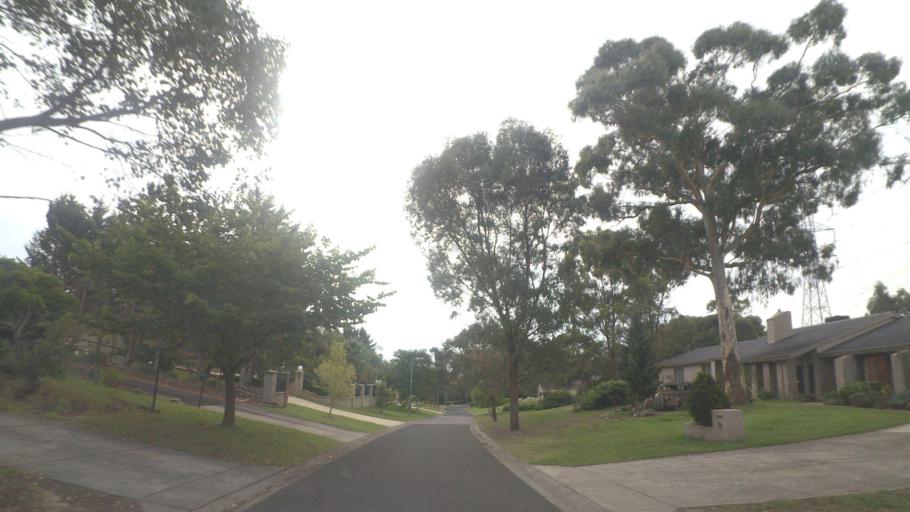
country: AU
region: Victoria
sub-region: Manningham
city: Donvale
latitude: -37.7643
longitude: 145.1880
